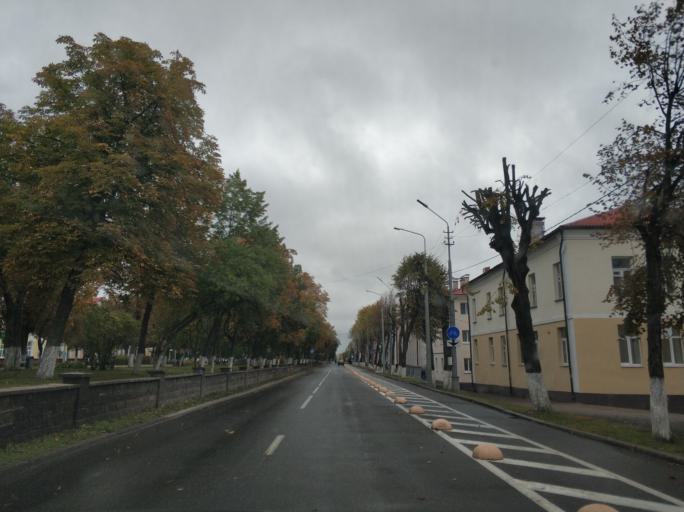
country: BY
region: Vitebsk
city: Polatsk
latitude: 55.4851
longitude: 28.7694
